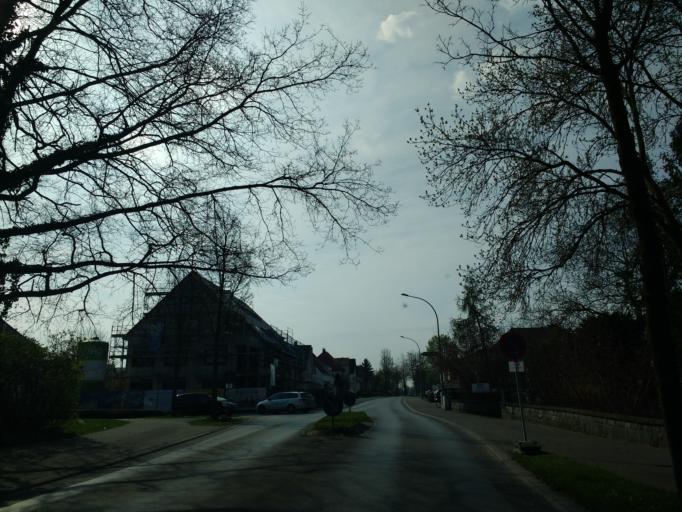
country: DE
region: North Rhine-Westphalia
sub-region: Regierungsbezirk Detmold
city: Salzkotten
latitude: 51.6688
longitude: 8.6004
